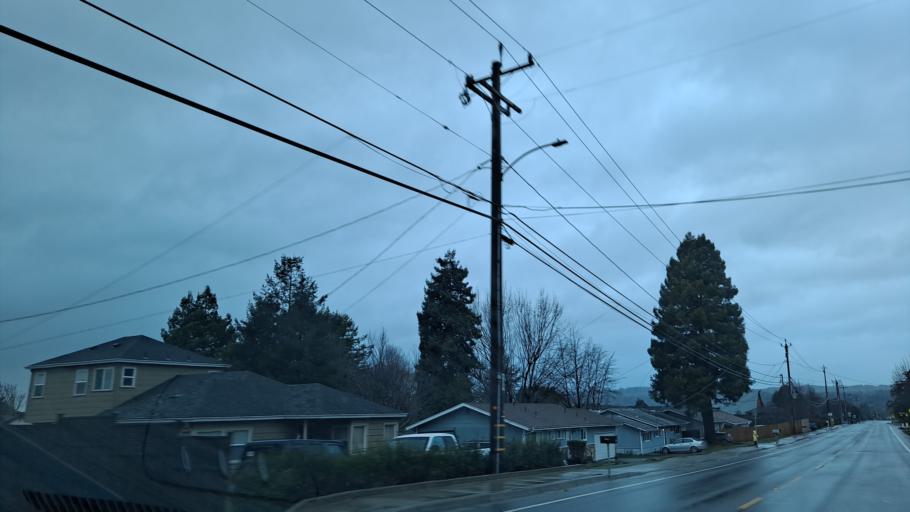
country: US
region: California
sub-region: Humboldt County
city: Fortuna
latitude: 40.5748
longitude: -124.1283
